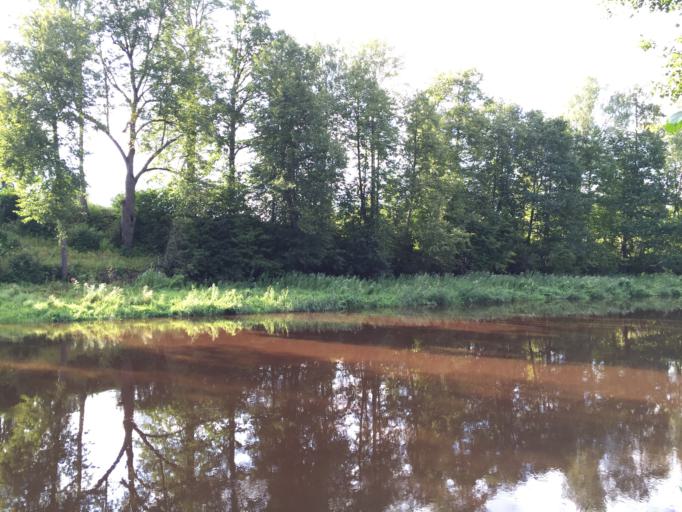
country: LV
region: Kegums
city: Kegums
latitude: 56.8168
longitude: 24.6948
